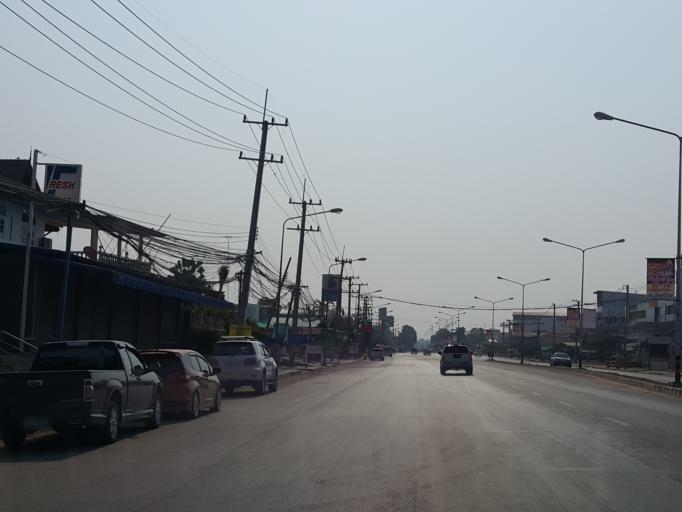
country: TH
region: Sukhothai
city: Sukhothai
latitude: 17.0096
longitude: 99.8012
